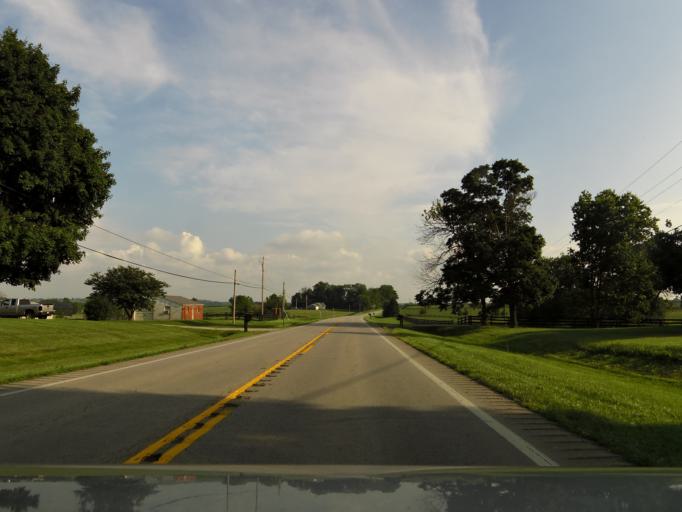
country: US
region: Kentucky
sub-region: Harrison County
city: Cynthiana
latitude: 38.3275
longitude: -84.3014
